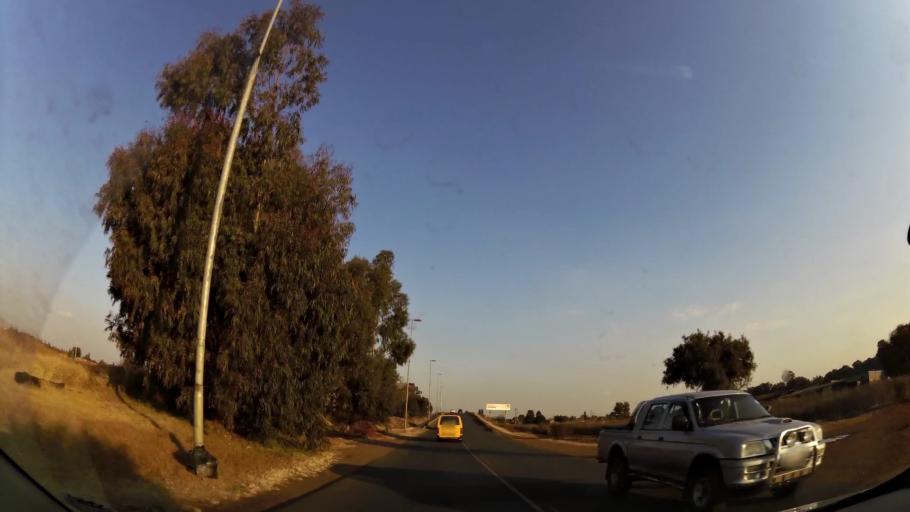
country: ZA
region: Gauteng
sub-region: Ekurhuleni Metropolitan Municipality
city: Germiston
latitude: -26.2998
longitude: 28.2316
